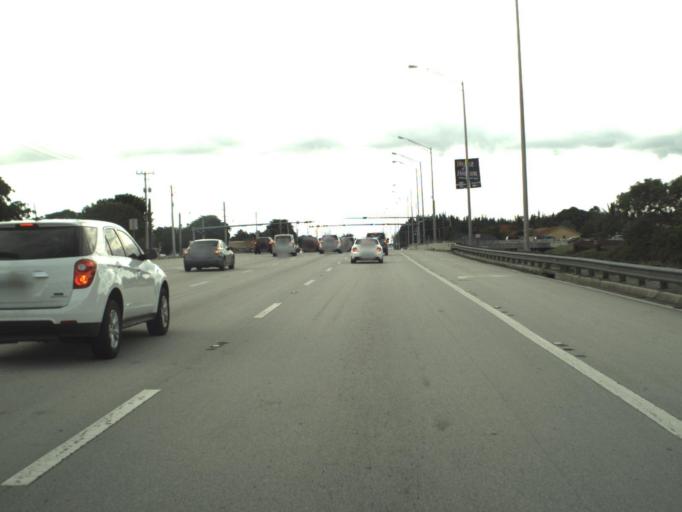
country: US
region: Florida
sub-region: Miami-Dade County
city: Tamiami
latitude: 25.7611
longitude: -80.4077
